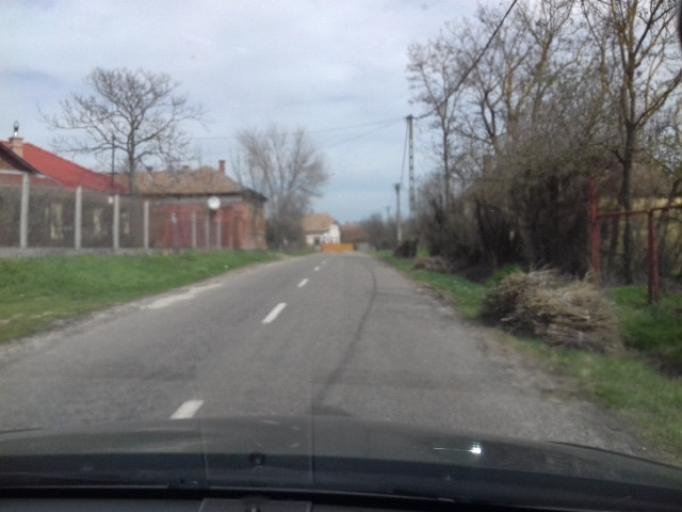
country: HU
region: Bacs-Kiskun
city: Tiszakecske
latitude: 46.9039
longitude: 20.1457
